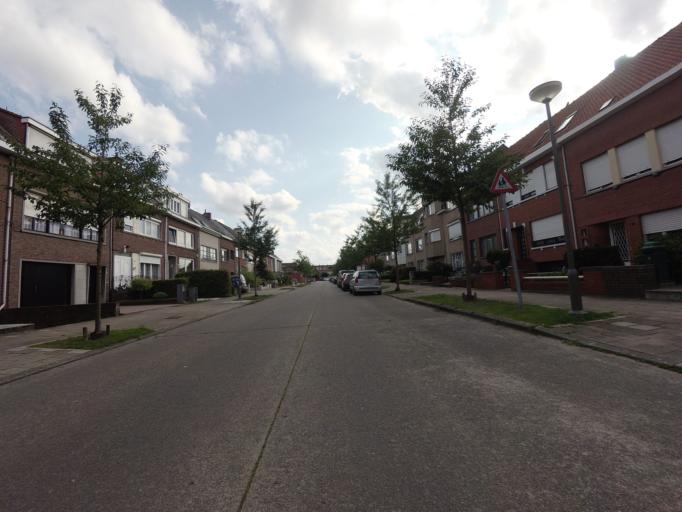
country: BE
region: Flanders
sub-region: Provincie Antwerpen
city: Aartselaar
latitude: 51.1693
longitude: 4.3906
